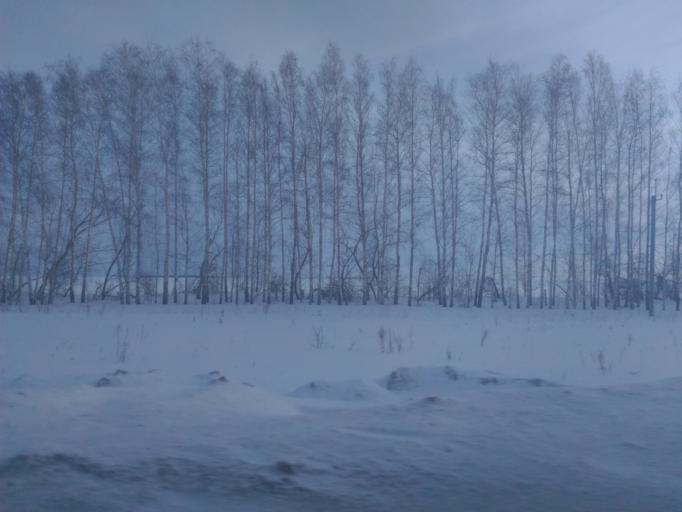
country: RU
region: Ulyanovsk
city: Isheyevka
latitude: 54.4104
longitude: 48.2957
